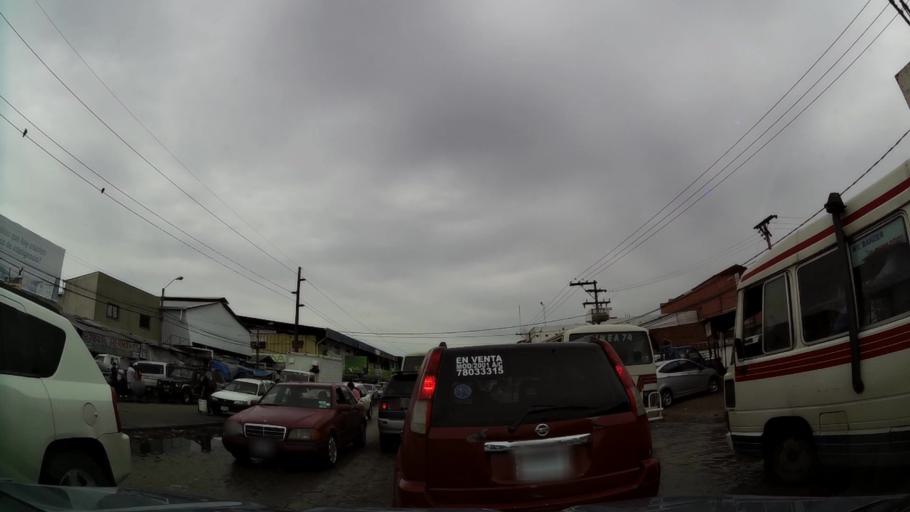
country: BO
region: Santa Cruz
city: Santa Cruz de la Sierra
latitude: -17.7633
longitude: -63.1627
